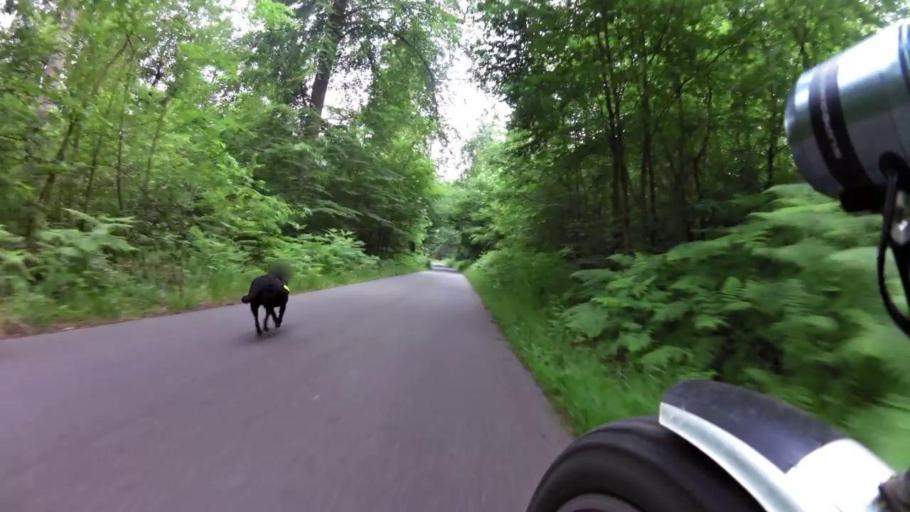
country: PL
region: West Pomeranian Voivodeship
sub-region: Powiat policki
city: Police
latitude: 53.6445
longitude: 14.4868
